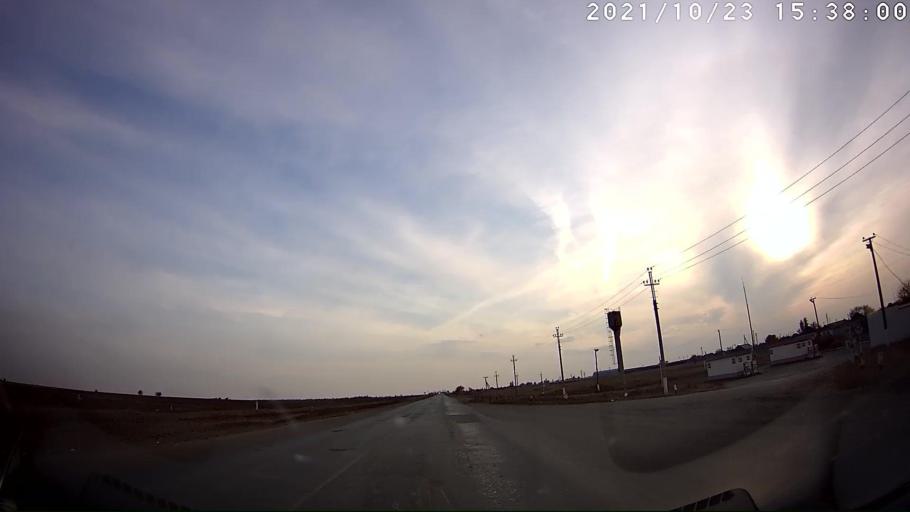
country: RU
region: Volgograd
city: Bereslavka
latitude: 48.1388
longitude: 44.1215
